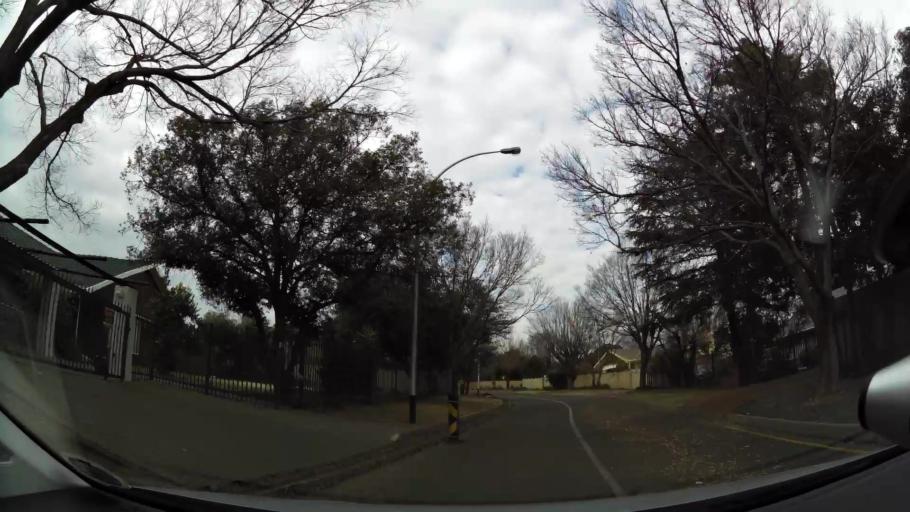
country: ZA
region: Orange Free State
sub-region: Mangaung Metropolitan Municipality
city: Bloemfontein
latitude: -29.0903
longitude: 26.2129
